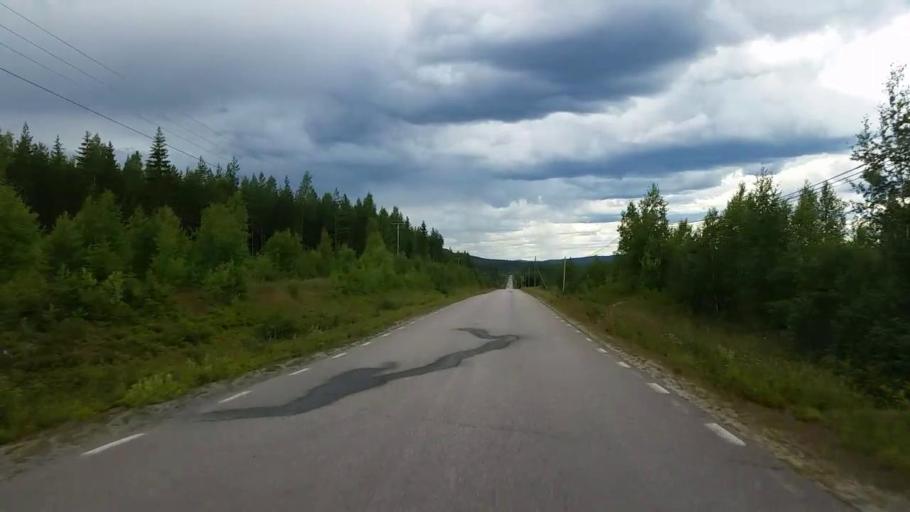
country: SE
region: Gaevleborg
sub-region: Ovanakers Kommun
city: Edsbyn
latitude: 61.4358
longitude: 15.8956
